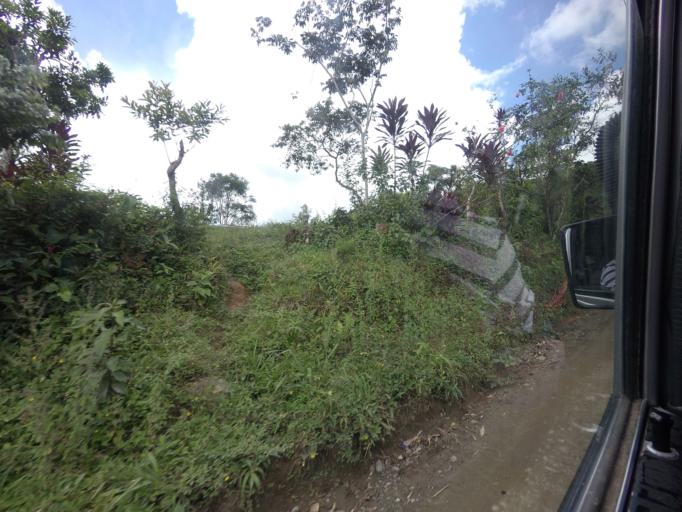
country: CO
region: Huila
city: Isnos
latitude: 1.9554
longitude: -76.2794
